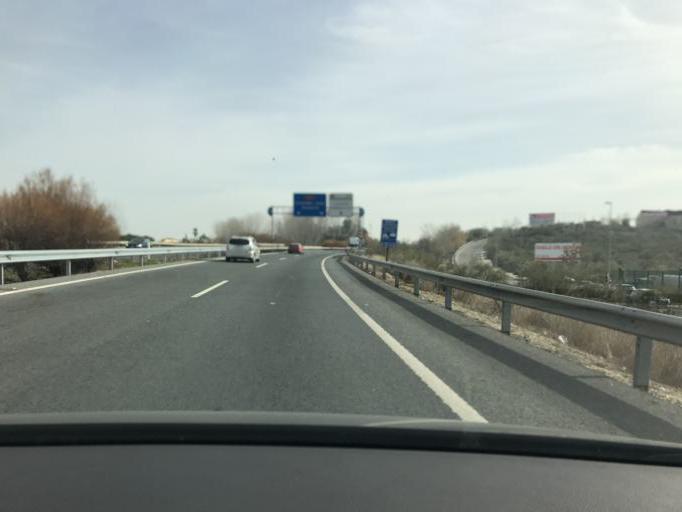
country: ES
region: Andalusia
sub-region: Provincia de Granada
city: Lachar
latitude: 37.1942
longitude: -3.8436
